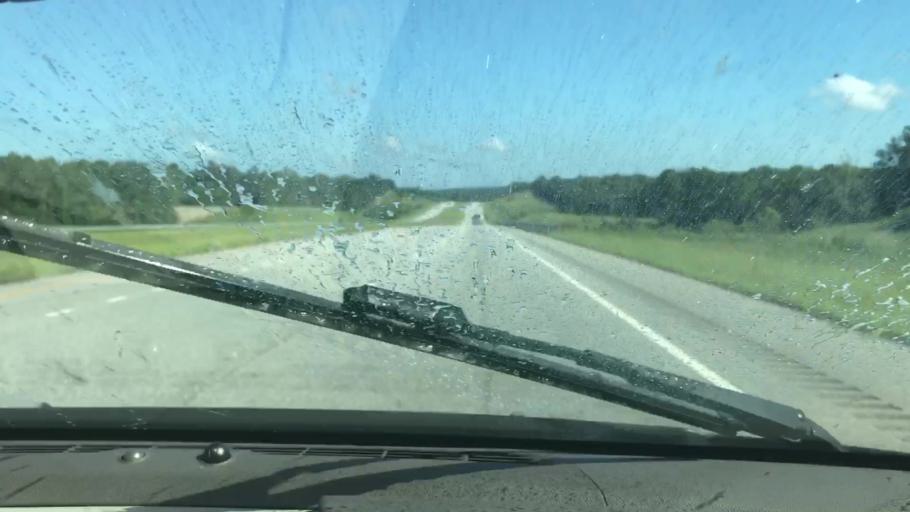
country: US
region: Alabama
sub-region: Barbour County
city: Eufaula
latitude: 32.0984
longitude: -85.1499
